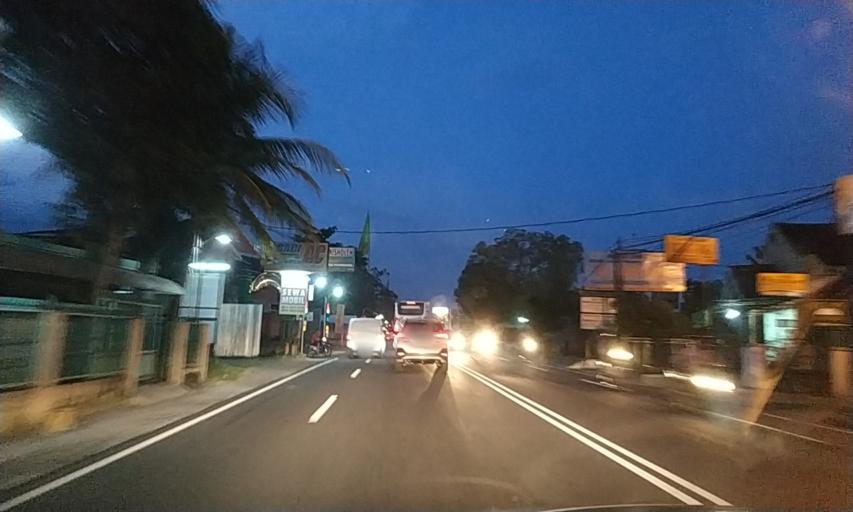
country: ID
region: Daerah Istimewa Yogyakarta
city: Godean
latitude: -7.8093
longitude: 110.2850
